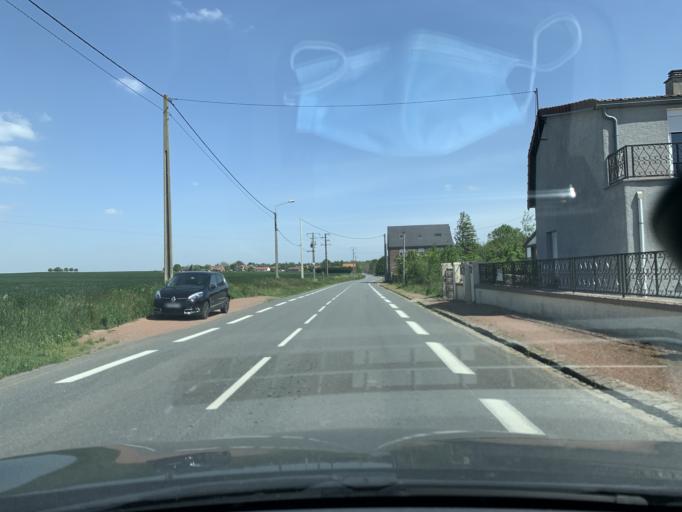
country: FR
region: Nord-Pas-de-Calais
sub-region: Departement du Nord
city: Marcoing
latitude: 50.1180
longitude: 3.1897
